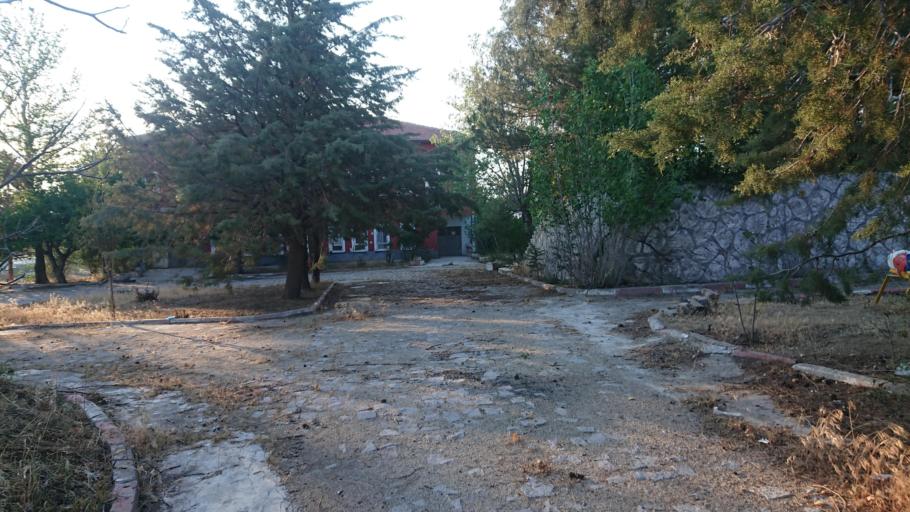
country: TR
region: Aksaray
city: Sariyahsi
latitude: 39.0257
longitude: 33.8926
